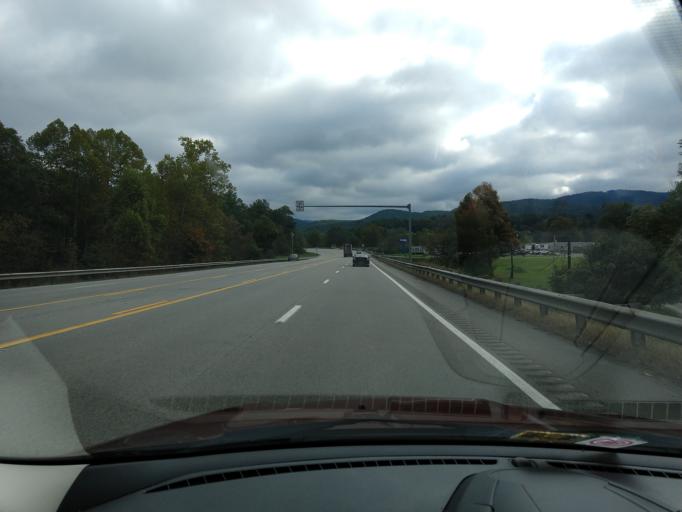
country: US
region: West Virginia
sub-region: Randolph County
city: Elkins
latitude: 38.8692
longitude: -79.8436
